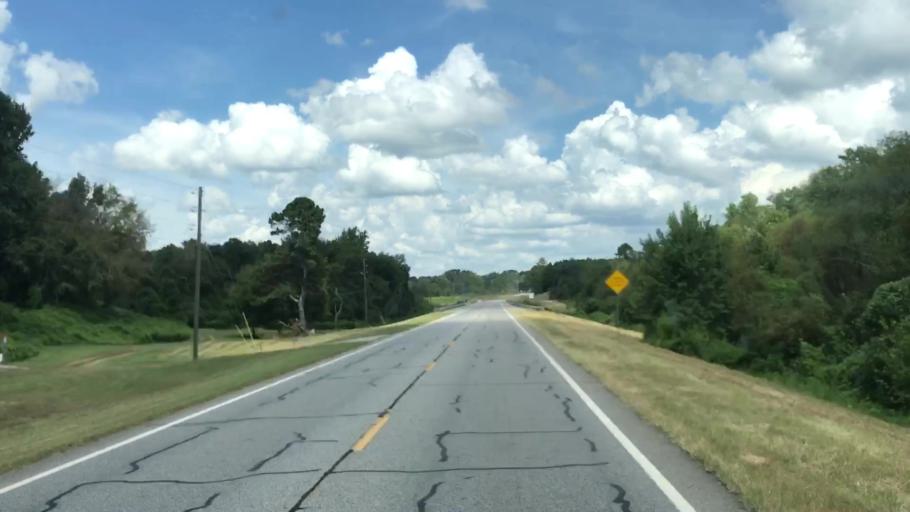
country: US
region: Georgia
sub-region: Oconee County
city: Watkinsville
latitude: 33.7328
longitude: -83.3030
